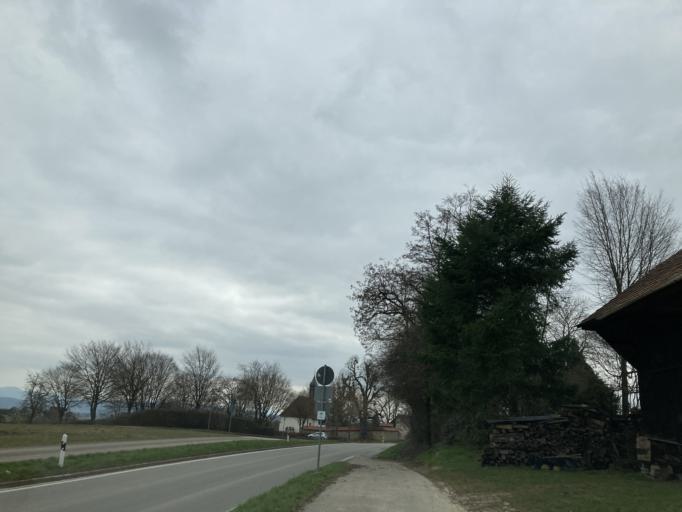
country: DE
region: Baden-Wuerttemberg
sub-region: Tuebingen Region
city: Hirrlingen
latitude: 48.4276
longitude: 8.8487
